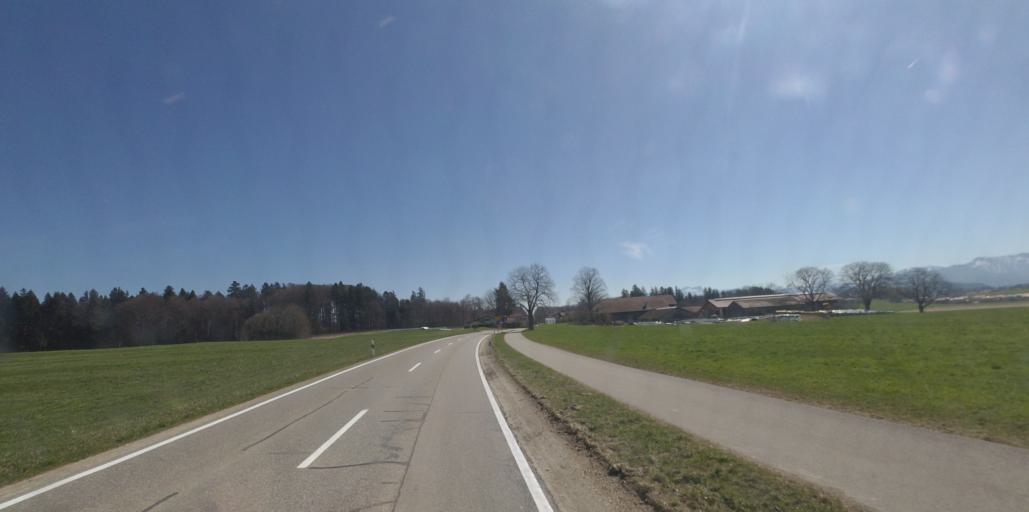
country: DE
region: Bavaria
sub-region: Upper Bavaria
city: Nussdorf
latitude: 47.8870
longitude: 12.6195
